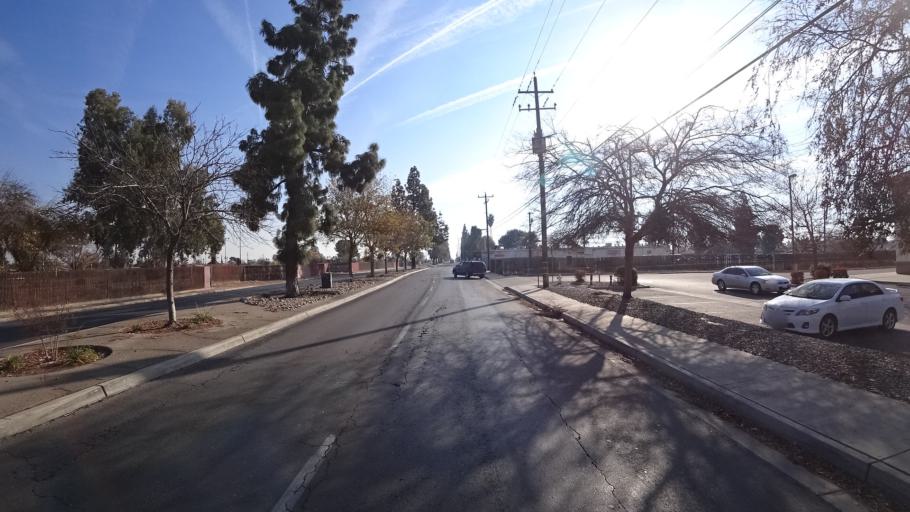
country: US
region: California
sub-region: Kern County
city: Bakersfield
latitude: 35.3244
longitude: -119.0214
